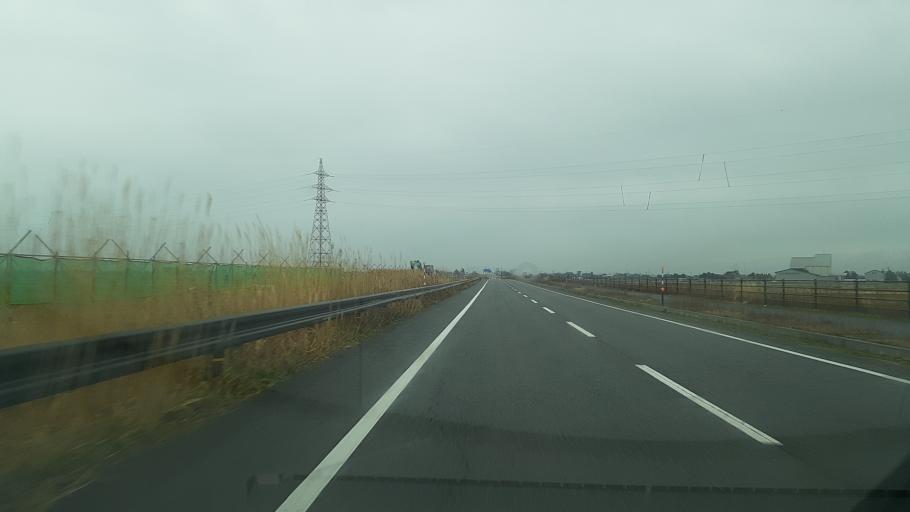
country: JP
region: Niigata
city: Kameda-honcho
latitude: 37.8710
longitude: 139.1492
